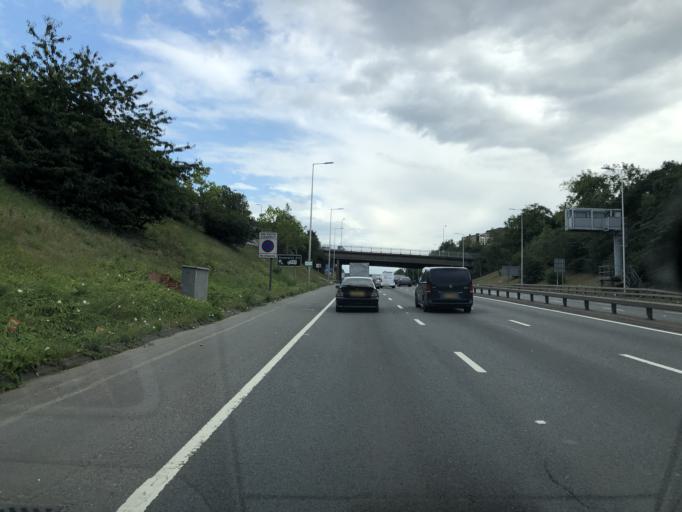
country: GB
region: England
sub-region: Greater London
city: Blackheath
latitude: 51.4800
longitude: 0.0218
